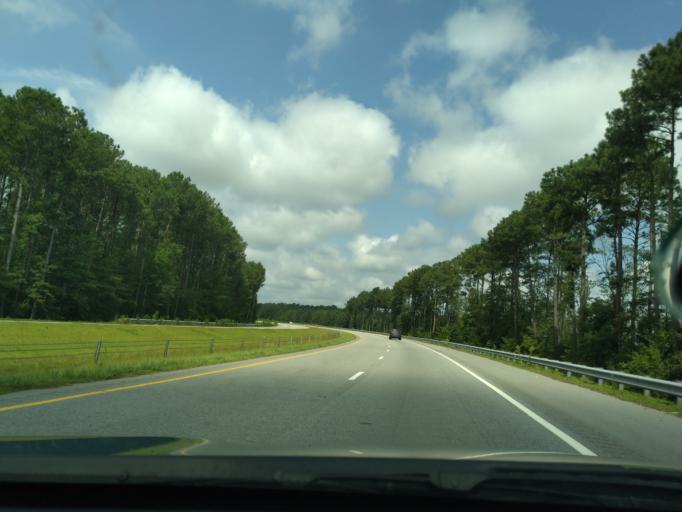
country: US
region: North Carolina
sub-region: Martin County
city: Williamston
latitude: 35.8295
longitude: -77.1129
